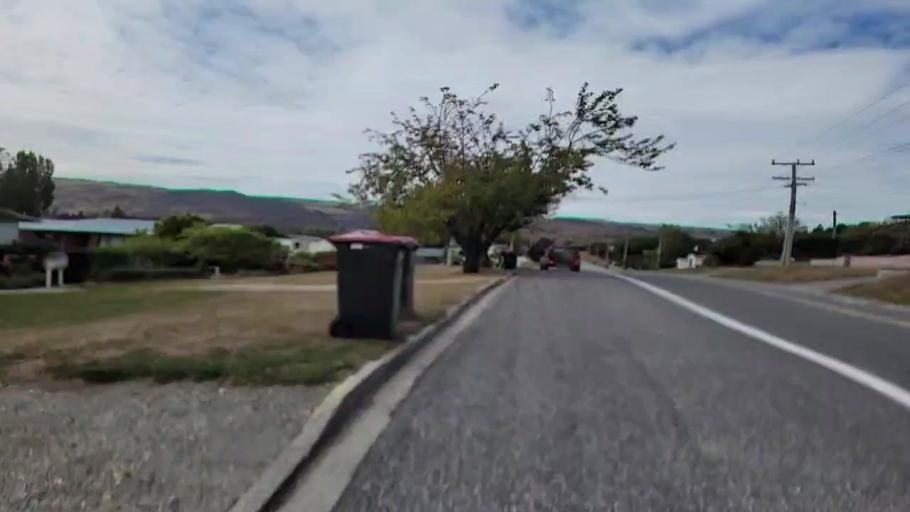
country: NZ
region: Otago
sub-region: Queenstown-Lakes District
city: Kingston
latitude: -45.5346
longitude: 169.3035
